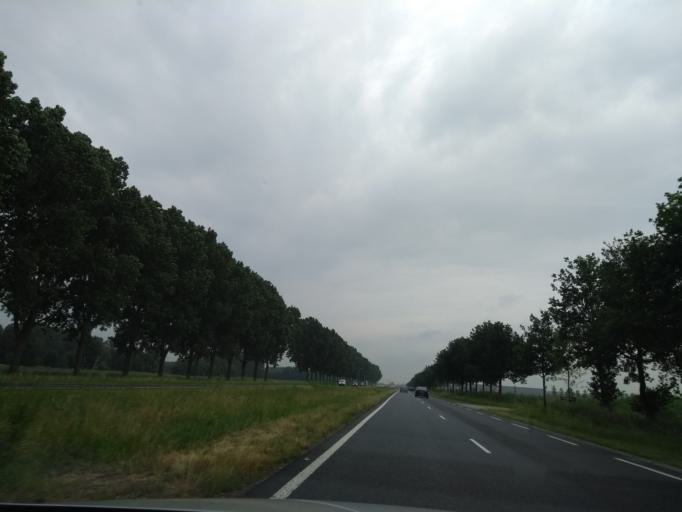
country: NL
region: North Holland
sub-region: Gemeente Huizen
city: Huizen
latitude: 52.3233
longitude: 5.3091
